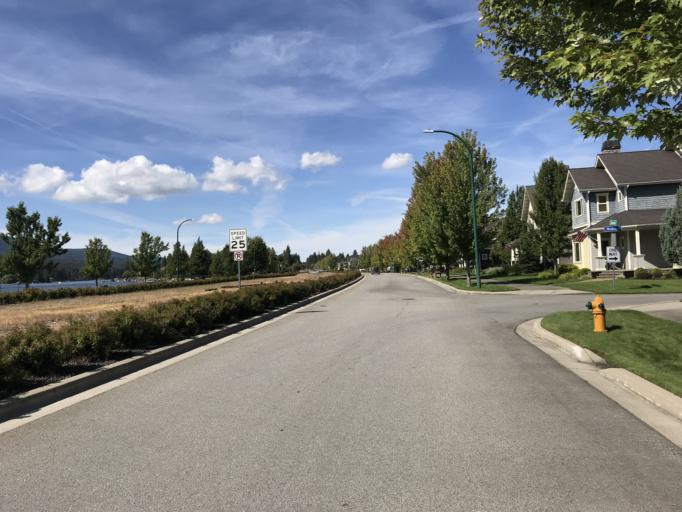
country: US
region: Idaho
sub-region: Kootenai County
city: Coeur d'Alene
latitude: 47.7008
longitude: -116.8408
